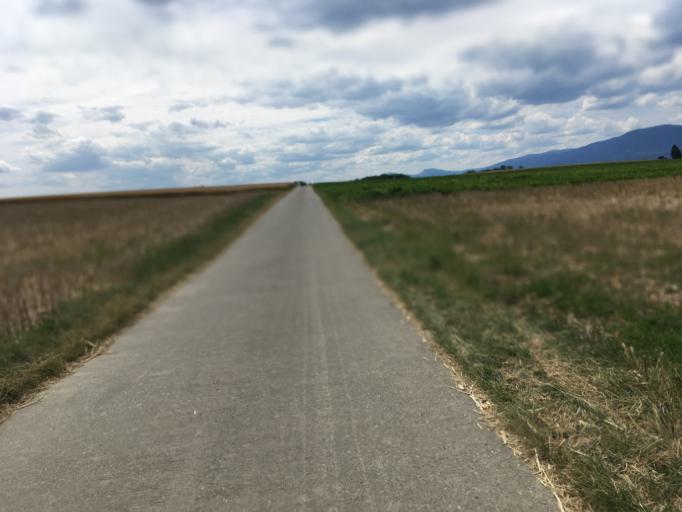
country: CH
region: Fribourg
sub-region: Broye District
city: Estavayer-le-Lac
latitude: 46.8605
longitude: 6.8738
